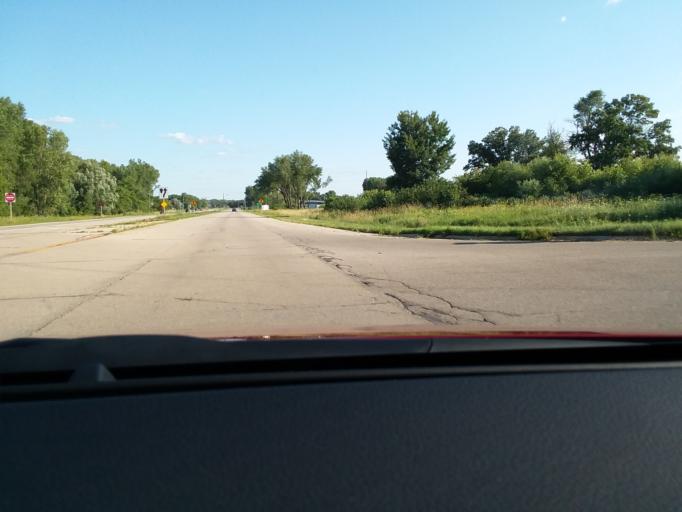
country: US
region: Wisconsin
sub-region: Dane County
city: Maple Bluff
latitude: 43.1630
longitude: -89.4065
